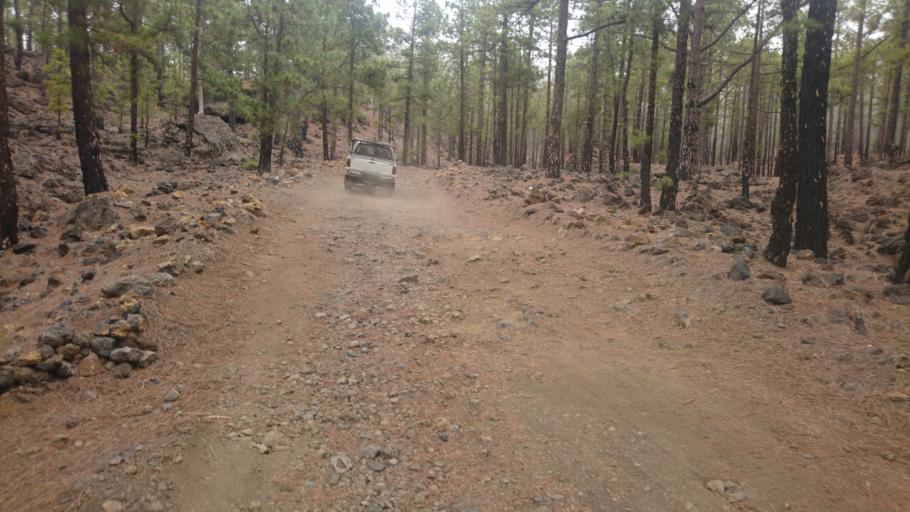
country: ES
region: Canary Islands
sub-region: Provincia de Santa Cruz de Tenerife
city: Guia de Isora
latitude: 28.2510
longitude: -16.7706
